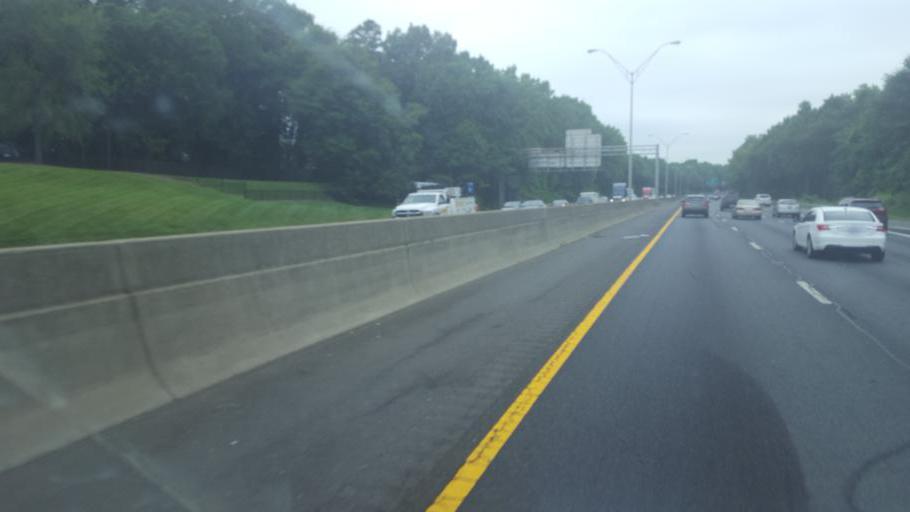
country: US
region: North Carolina
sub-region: Mecklenburg County
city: Charlotte
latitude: 35.1995
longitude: -80.8819
